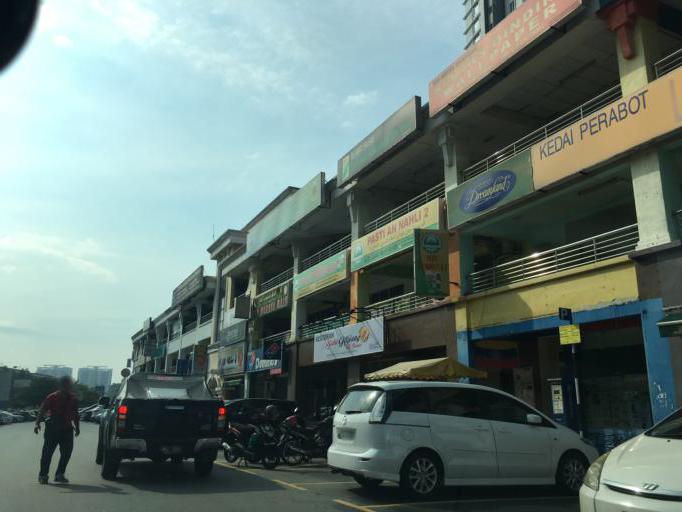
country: MY
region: Kuala Lumpur
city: Kuala Lumpur
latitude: 3.2245
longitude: 101.7294
